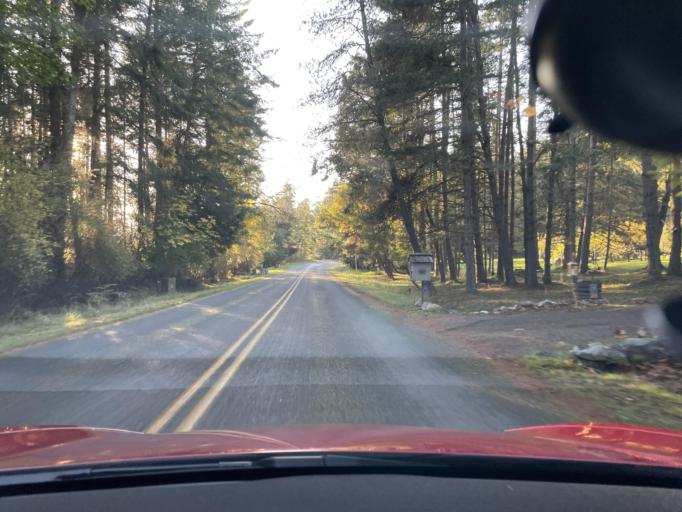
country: US
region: Washington
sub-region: San Juan County
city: Friday Harbor
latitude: 48.5507
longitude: -123.1615
